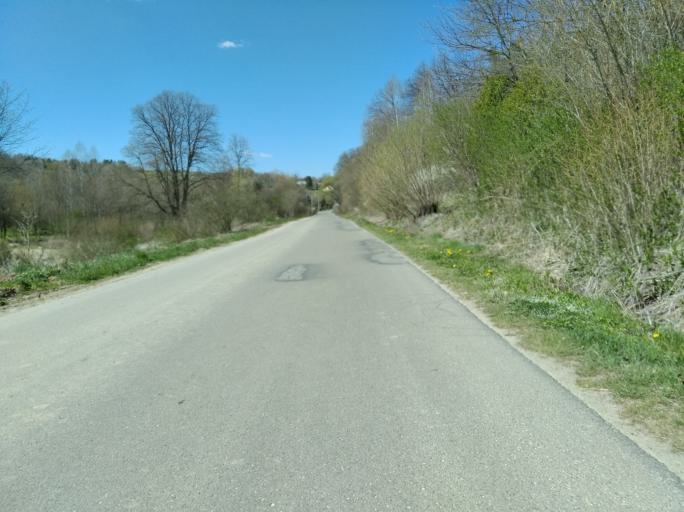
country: PL
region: Subcarpathian Voivodeship
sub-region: Powiat brzozowski
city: Dydnia
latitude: 49.7068
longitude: 22.1479
